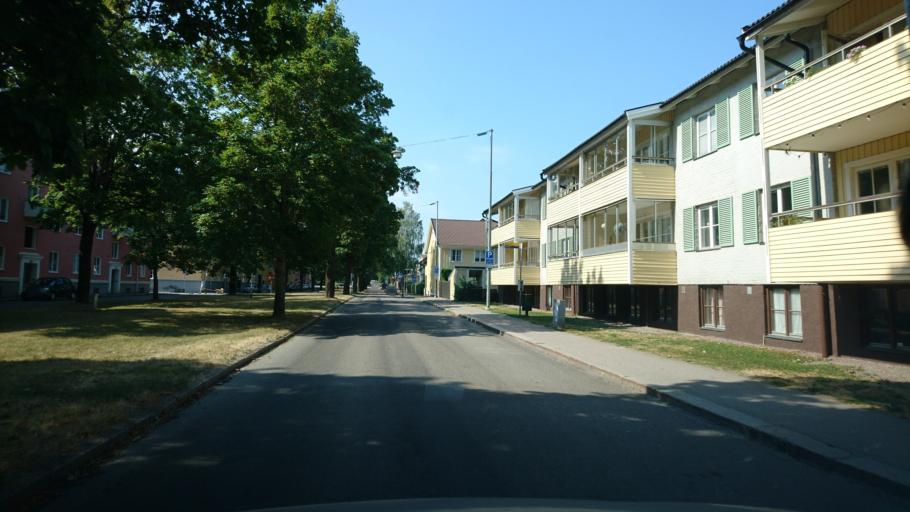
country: SE
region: Uppsala
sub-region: Uppsala Kommun
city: Uppsala
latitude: 59.8647
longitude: 17.6181
